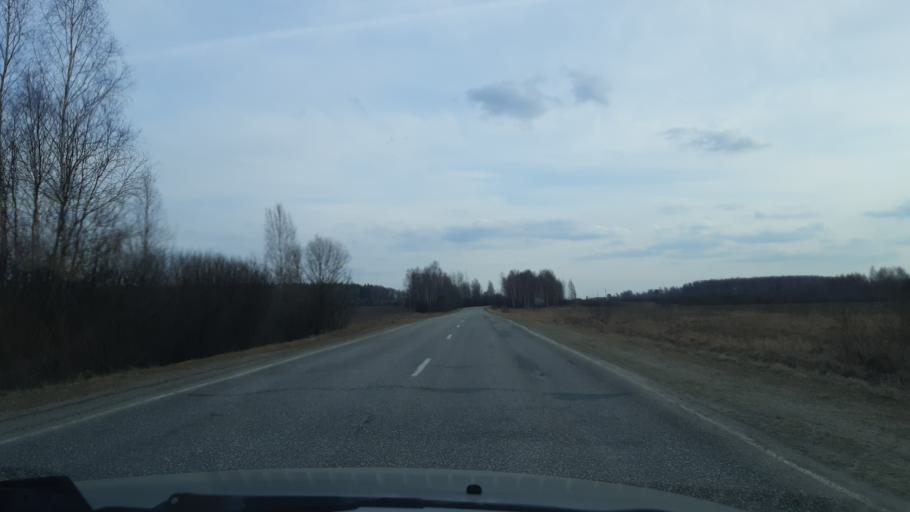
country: RU
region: Vladimir
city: Luknovo
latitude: 56.2108
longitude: 42.0317
